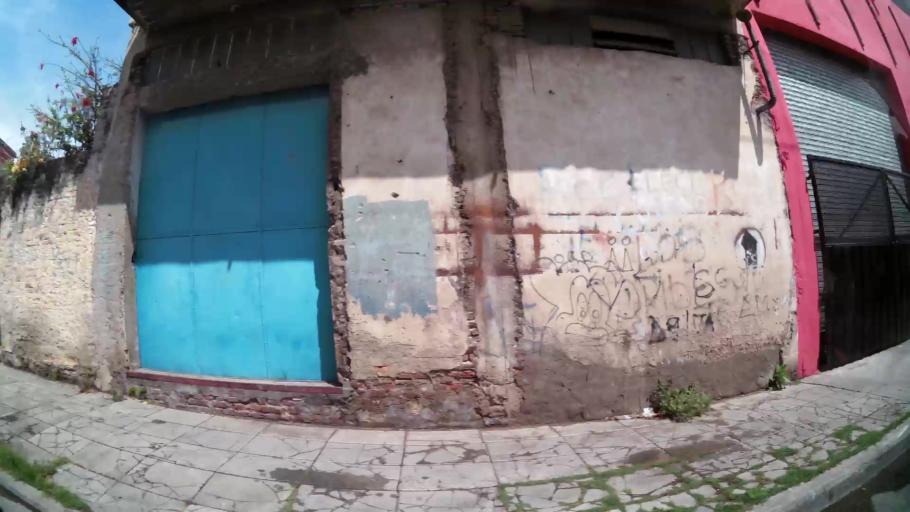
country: AR
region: Buenos Aires F.D.
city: Villa Lugano
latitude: -34.6606
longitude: -58.4366
